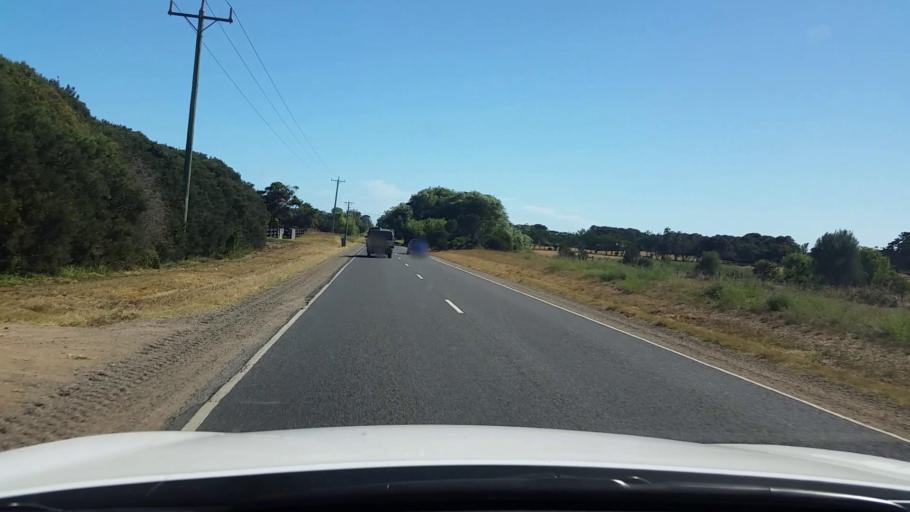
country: AU
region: Victoria
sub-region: Mornington Peninsula
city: Rosebud West
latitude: -38.4067
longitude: 144.8877
